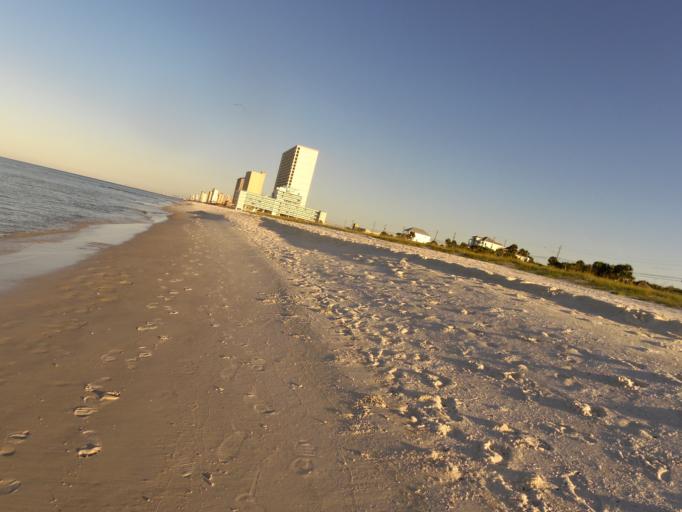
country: US
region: Florida
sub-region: Bay County
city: Panama City Beach
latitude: 30.2009
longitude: -85.8516
